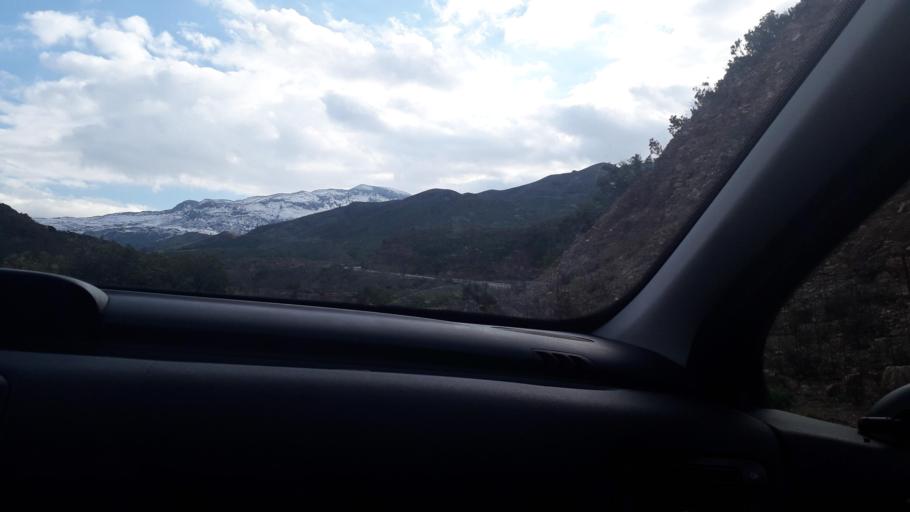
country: GR
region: Crete
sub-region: Nomos Rethymnis
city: Agia Foteini
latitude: 35.2797
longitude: 24.5624
